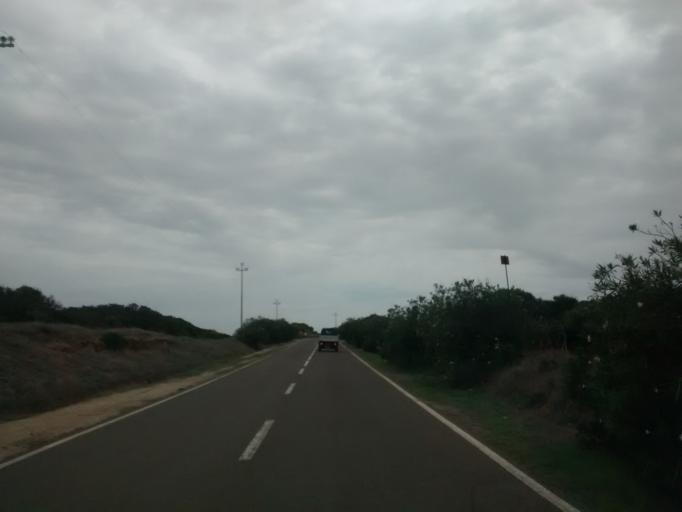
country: IT
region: Sardinia
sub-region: Provincia di Cagliari
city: Villasimius
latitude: 39.1141
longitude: 9.5085
